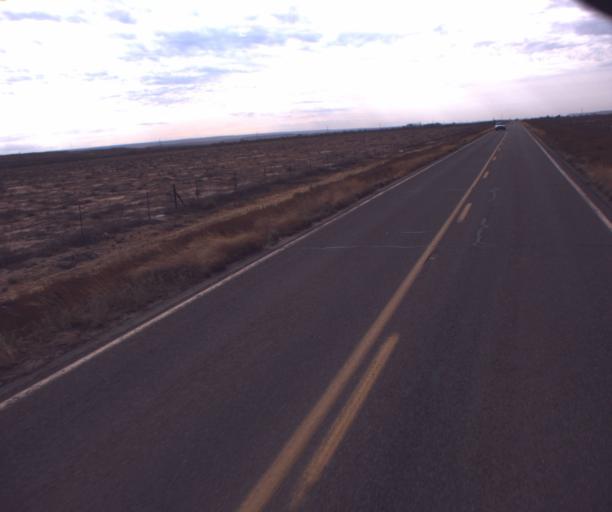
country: US
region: Arizona
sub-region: Apache County
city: Many Farms
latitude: 36.4527
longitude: -109.6079
